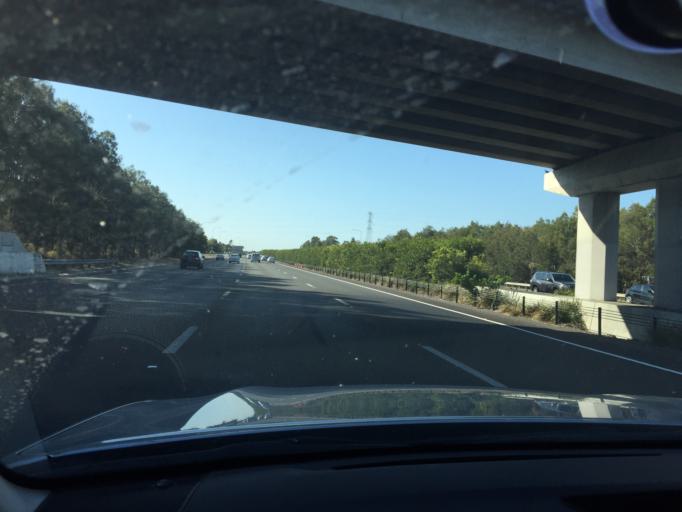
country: AU
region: Queensland
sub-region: Gold Coast
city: Yatala
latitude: -27.7201
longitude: 153.2137
